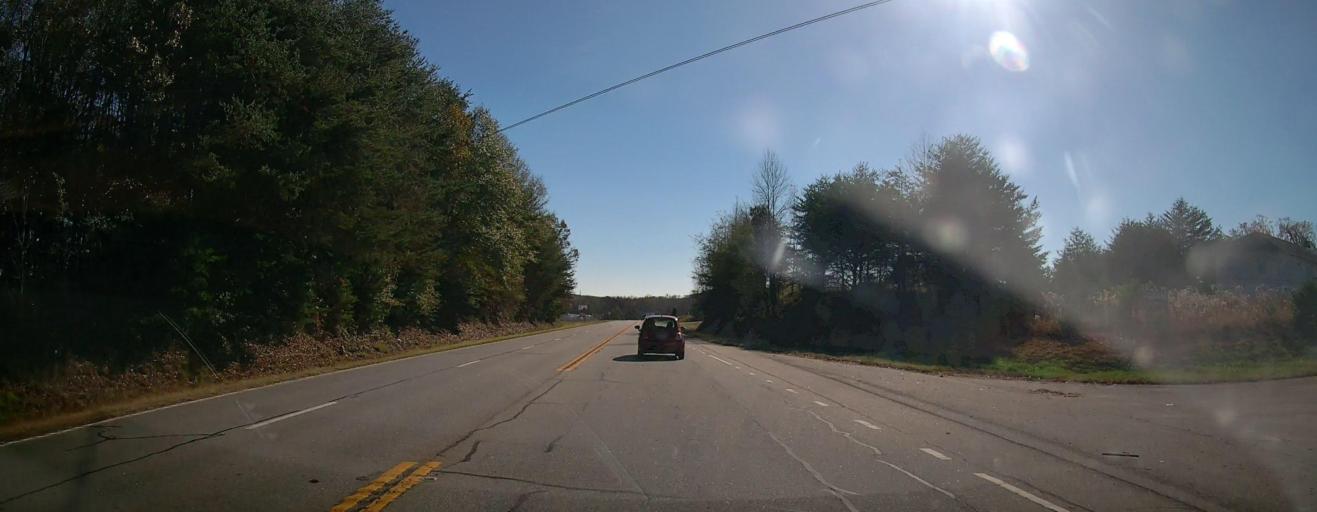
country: US
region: Georgia
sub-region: White County
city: Cleveland
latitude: 34.5110
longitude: -83.7558
